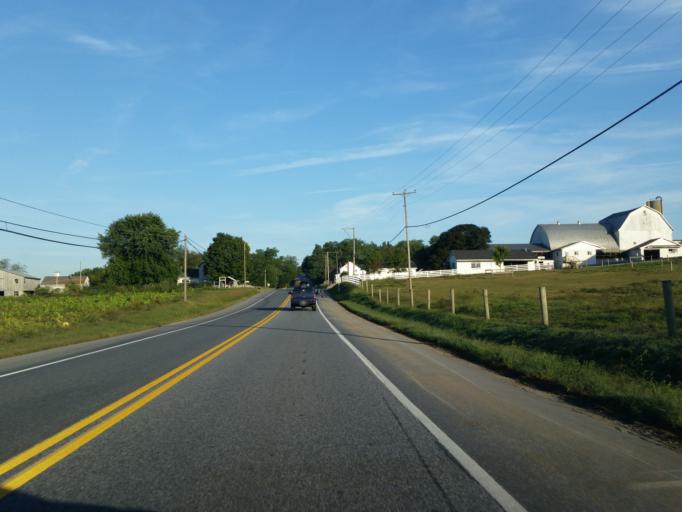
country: US
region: Pennsylvania
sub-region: Lancaster County
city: Quarryville
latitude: 39.8167
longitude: -76.1921
